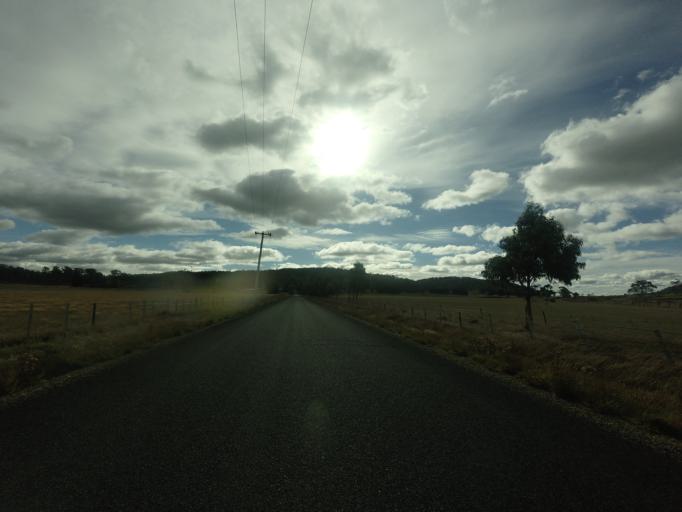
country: AU
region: Tasmania
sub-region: Brighton
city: Bridgewater
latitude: -42.4015
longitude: 147.3899
